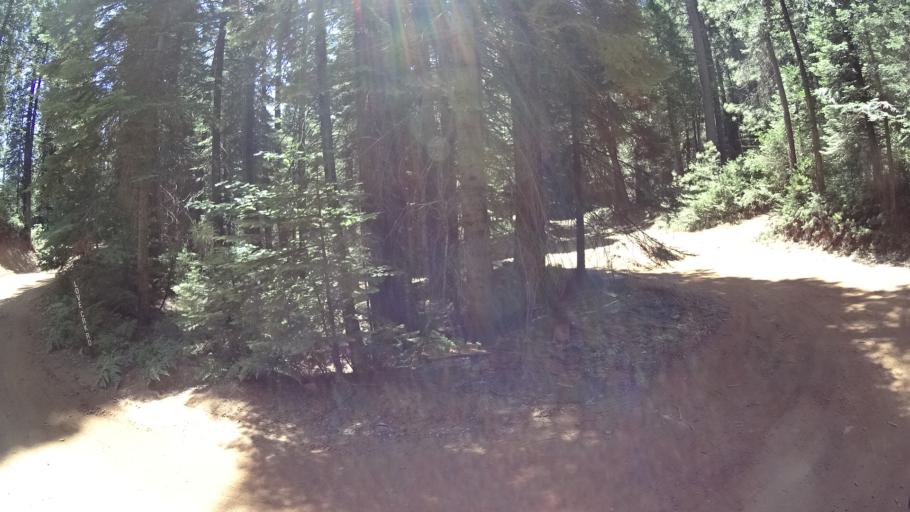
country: US
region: California
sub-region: Calaveras County
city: Arnold
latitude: 38.2535
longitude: -120.3073
